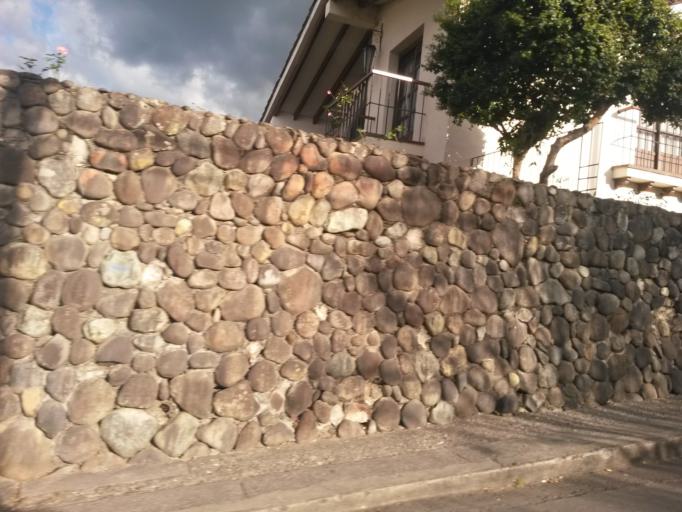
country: CO
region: Cauca
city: Popayan
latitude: 2.4581
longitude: -76.5956
